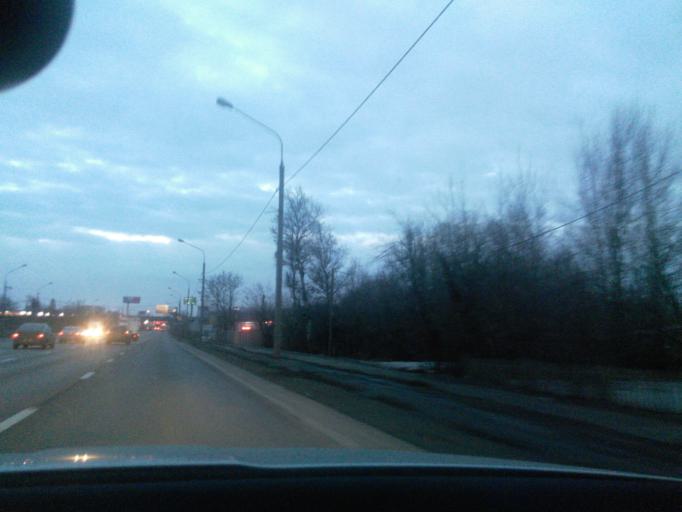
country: RU
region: Moskovskaya
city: Novopodrezkovo
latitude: 55.9233
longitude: 37.3887
